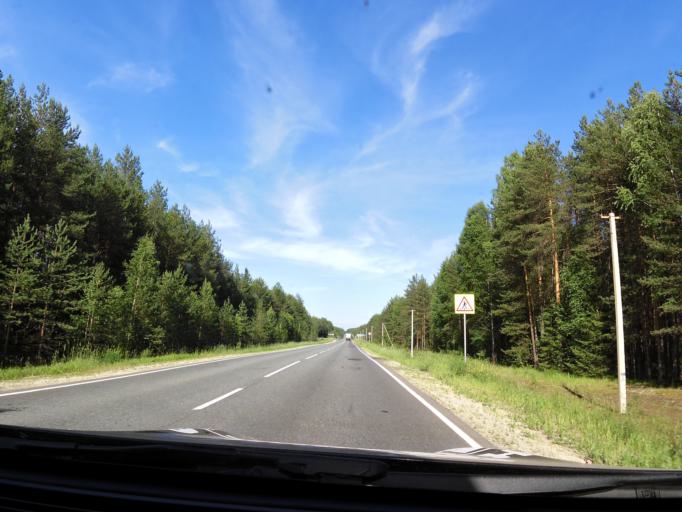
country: RU
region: Kirov
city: Belaya Kholunitsa
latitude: 58.9108
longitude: 51.0634
